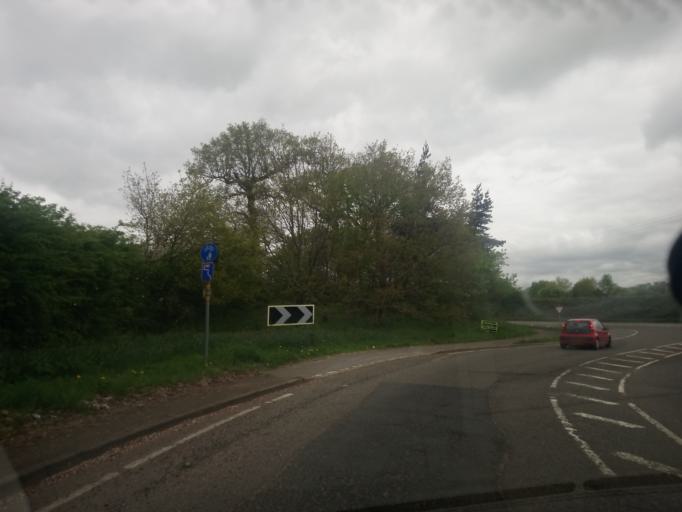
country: GB
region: England
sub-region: Telford and Wrekin
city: Chetwynd
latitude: 52.7895
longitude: -2.3945
